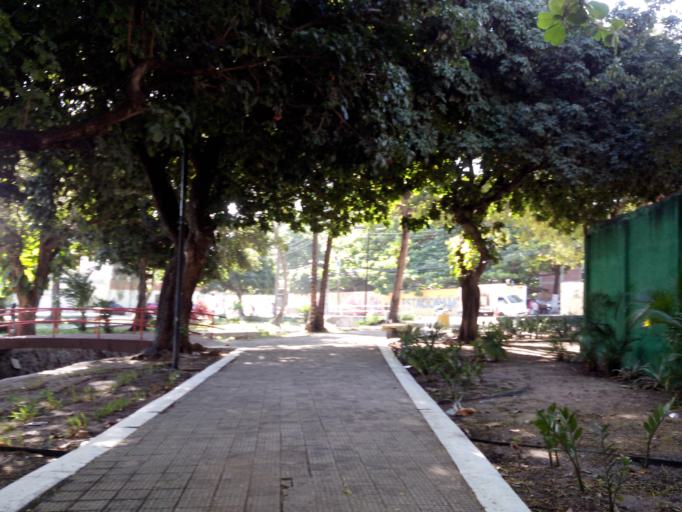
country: BR
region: Ceara
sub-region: Fortaleza
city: Fortaleza
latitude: -3.7308
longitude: -38.5235
